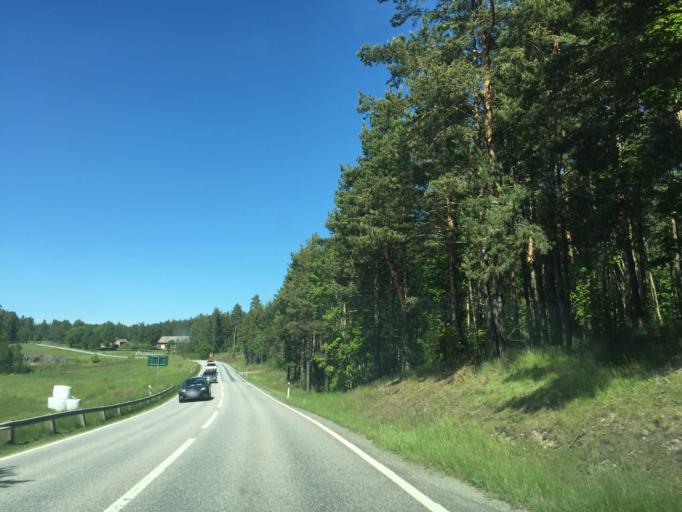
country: SE
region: OEstergoetland
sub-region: Motala Kommun
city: Ryd
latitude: 58.6942
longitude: 14.9672
